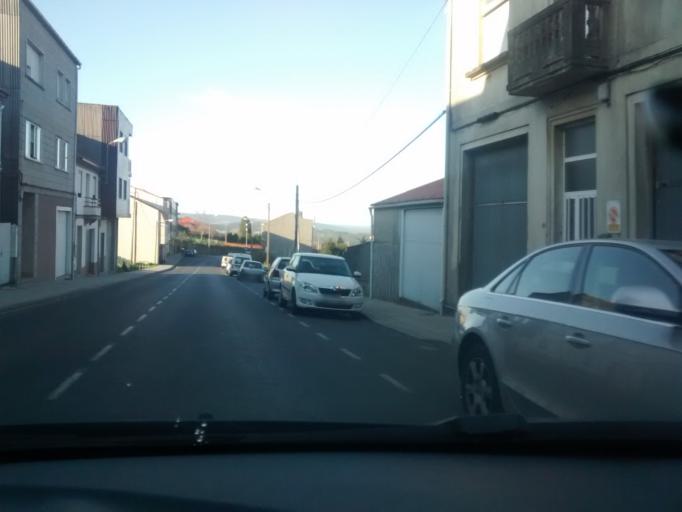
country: ES
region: Galicia
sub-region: Provincia de Pontevedra
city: A Estrada
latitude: 42.6919
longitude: -8.4850
